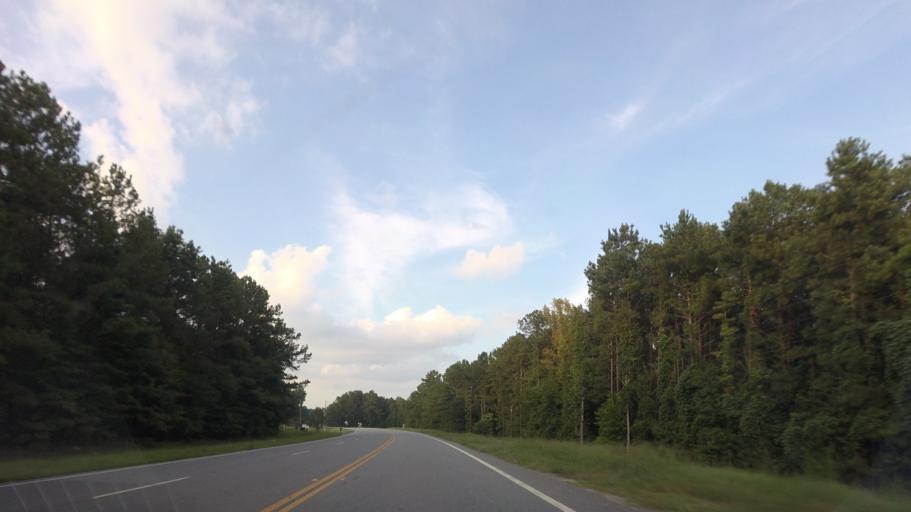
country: US
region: Georgia
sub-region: Wilkinson County
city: Gordon
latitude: 32.8681
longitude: -83.3434
